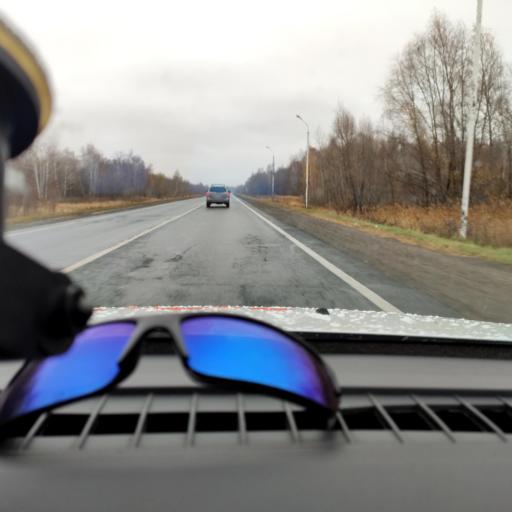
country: RU
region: Samara
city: Chapayevsk
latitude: 52.9940
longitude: 49.8195
